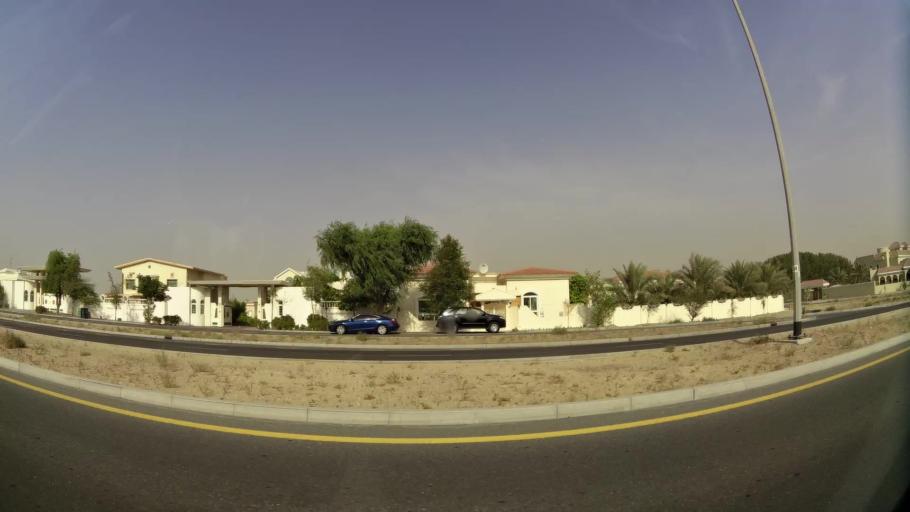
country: AE
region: Ash Shariqah
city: Sharjah
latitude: 25.2405
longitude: 55.4526
